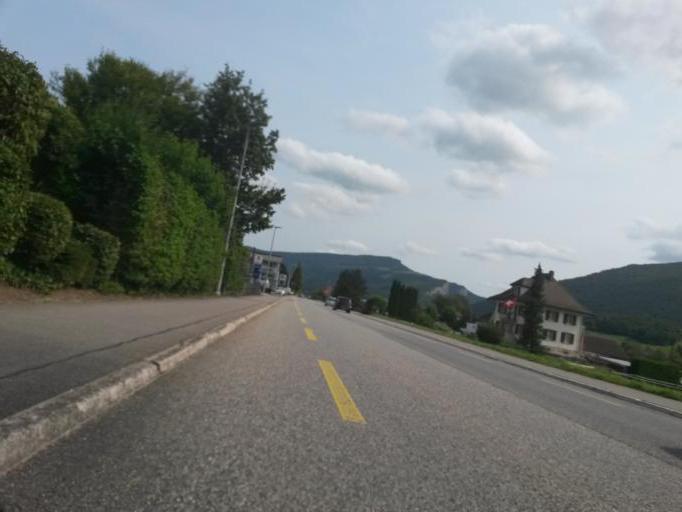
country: CH
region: Solothurn
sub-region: Bezirk Thal
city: Laupersdorf
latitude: 47.3120
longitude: 7.6539
